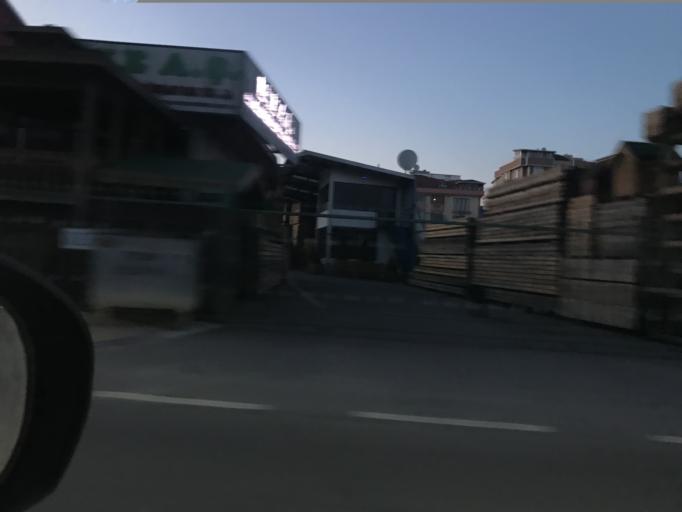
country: TR
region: Istanbul
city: Pendik
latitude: 40.9064
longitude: 29.2881
